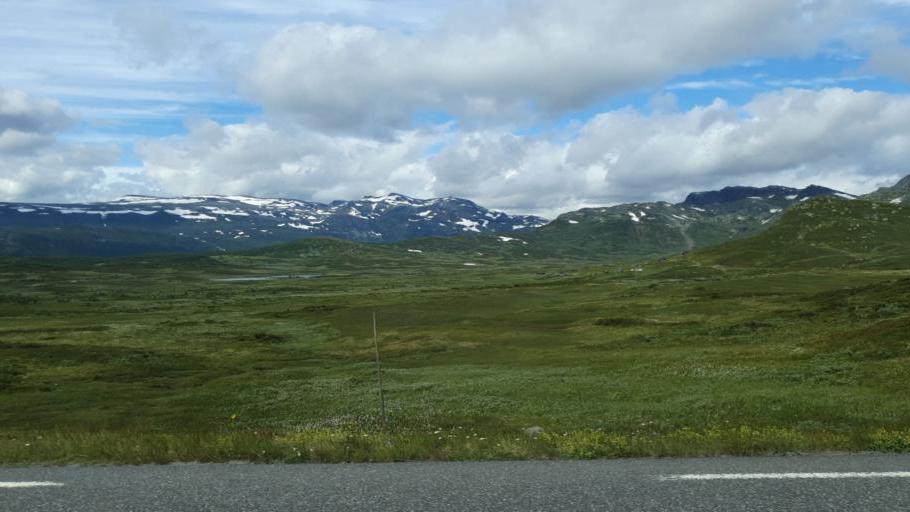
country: NO
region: Oppland
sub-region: Vestre Slidre
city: Slidre
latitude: 61.2752
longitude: 8.8568
